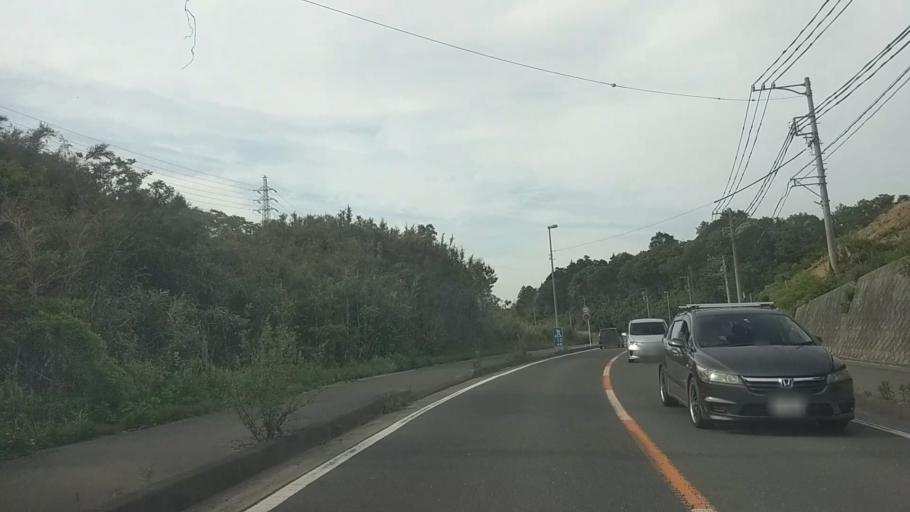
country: JP
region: Shizuoka
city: Hamamatsu
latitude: 34.7498
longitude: 137.6539
